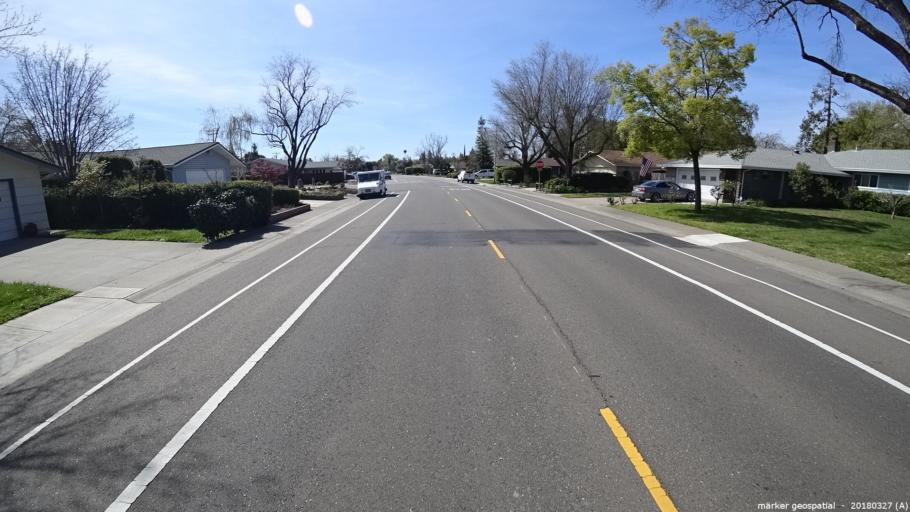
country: US
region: California
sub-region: Sacramento County
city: Rosemont
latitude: 38.5496
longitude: -121.3665
